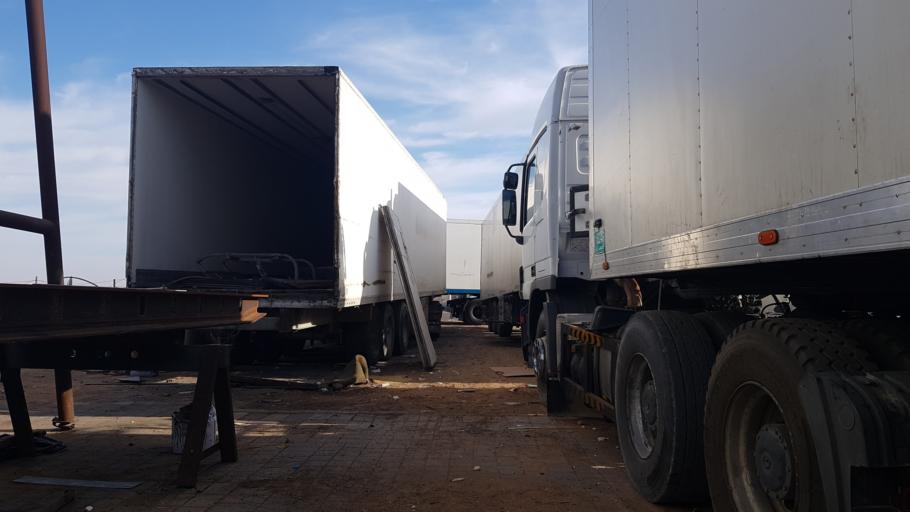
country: AE
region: Ash Shariqah
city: Adh Dhayd
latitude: 24.9298
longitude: 55.7520
